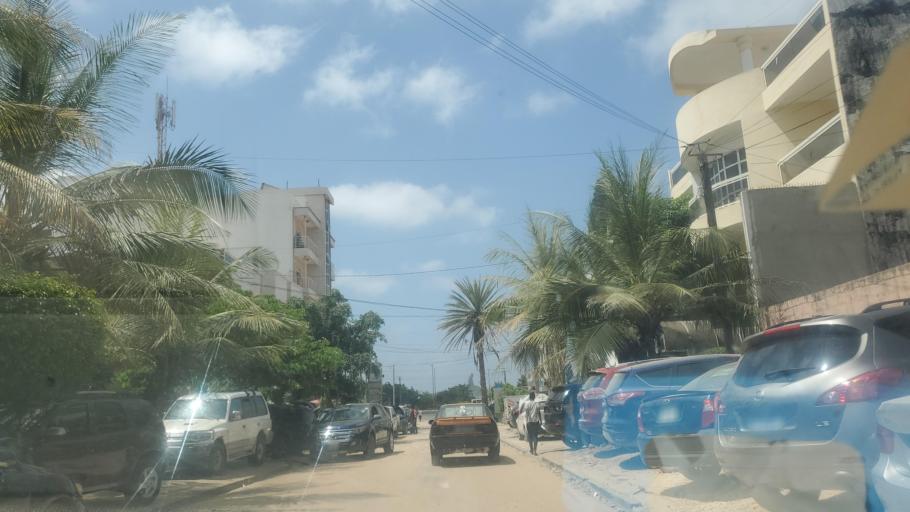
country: SN
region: Dakar
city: Grand Dakar
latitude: 14.7294
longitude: -17.4712
